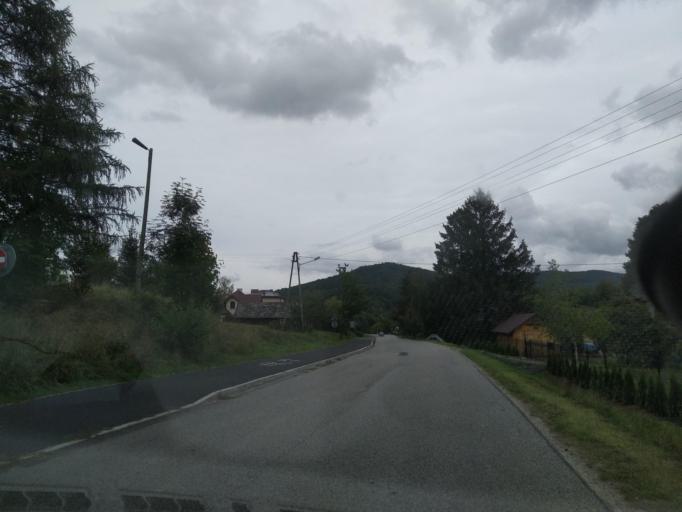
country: PL
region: Lesser Poland Voivodeship
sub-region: Powiat gorlicki
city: Lipinki
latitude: 49.6247
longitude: 21.2715
